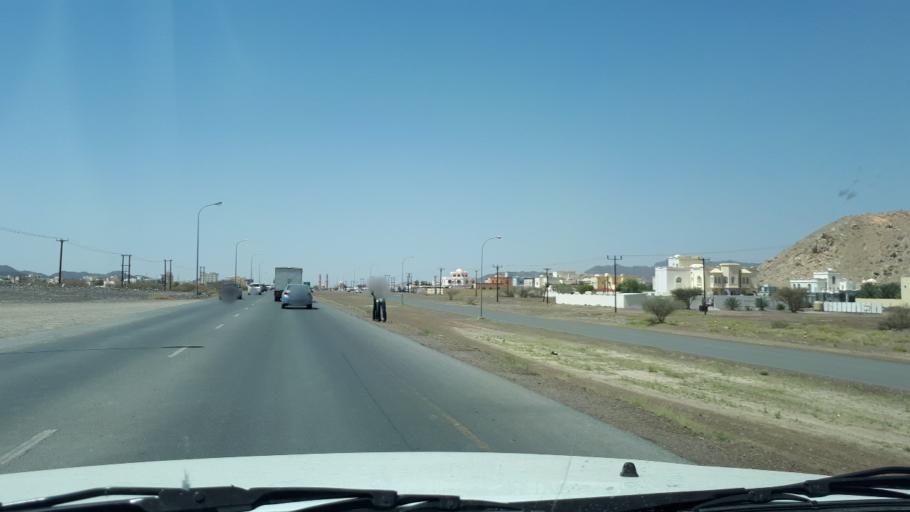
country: OM
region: Muhafazat ad Dakhiliyah
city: Bahla'
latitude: 23.0092
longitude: 57.3235
